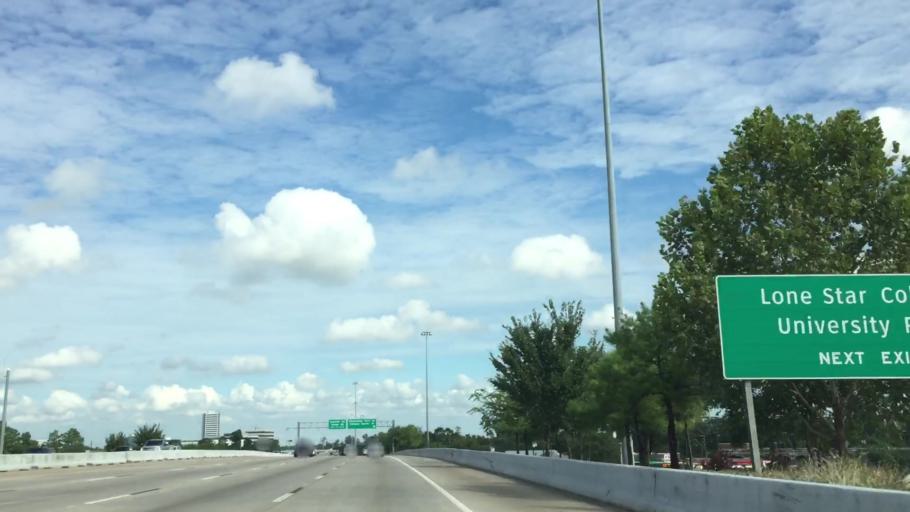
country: US
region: Texas
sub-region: Harris County
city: Oak Cliff Place
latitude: 29.9806
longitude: -95.5668
